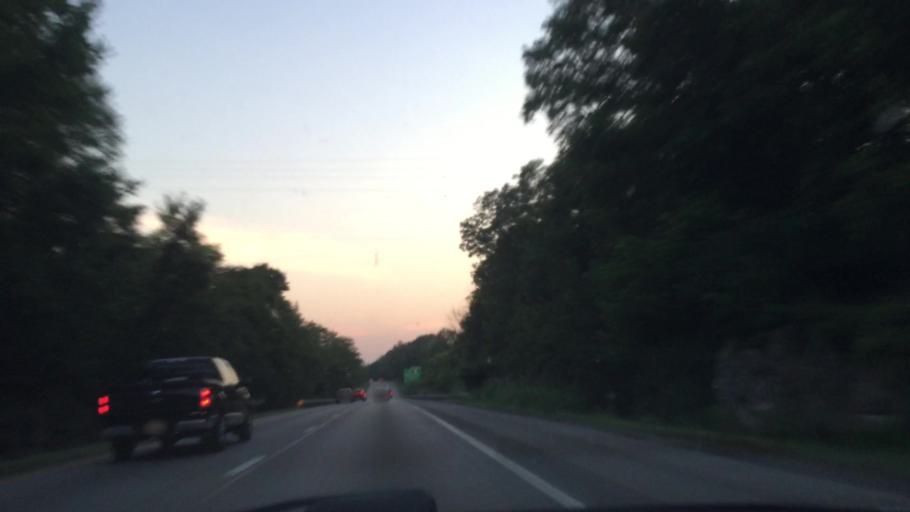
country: US
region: Kentucky
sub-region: Oldham County
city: Orchard Grass Hills
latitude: 38.3338
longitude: -85.5346
